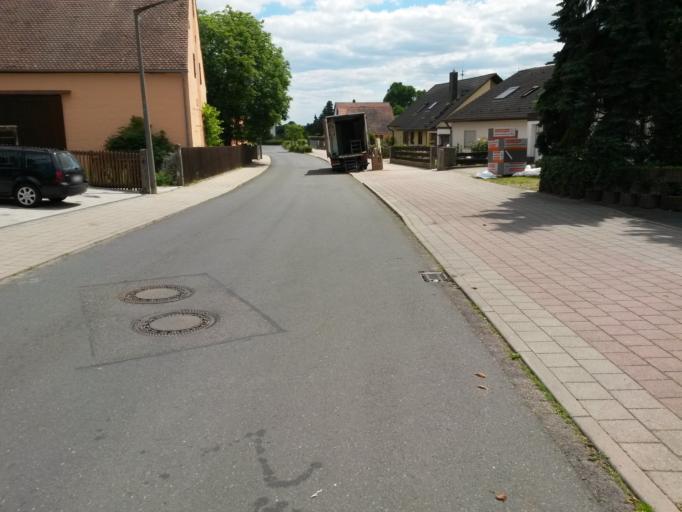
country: DE
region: Bavaria
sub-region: Regierungsbezirk Mittelfranken
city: Zirndorf
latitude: 49.4717
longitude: 10.9396
